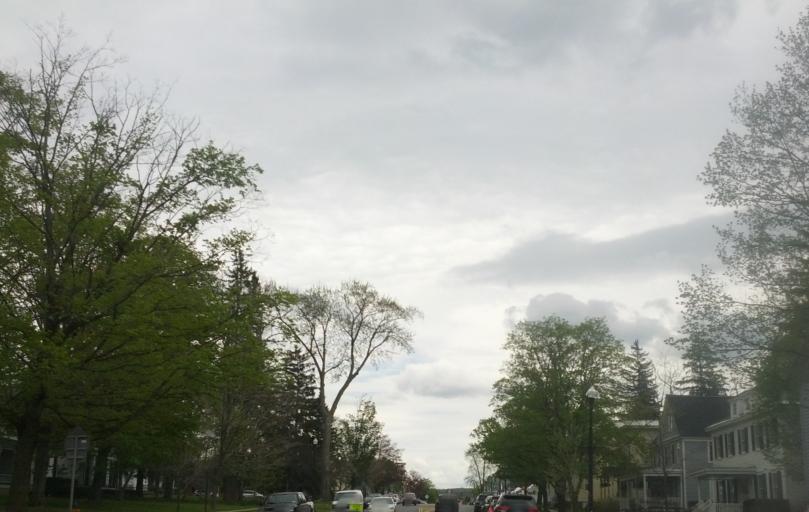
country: US
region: New York
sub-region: Madison County
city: Cazenovia
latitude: 42.9299
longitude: -75.8575
